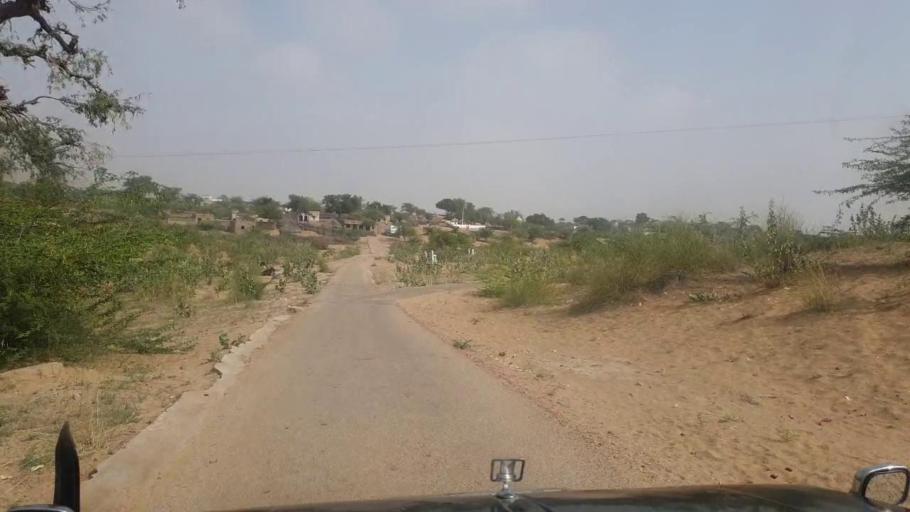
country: PK
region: Sindh
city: Islamkot
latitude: 25.1315
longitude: 70.1443
